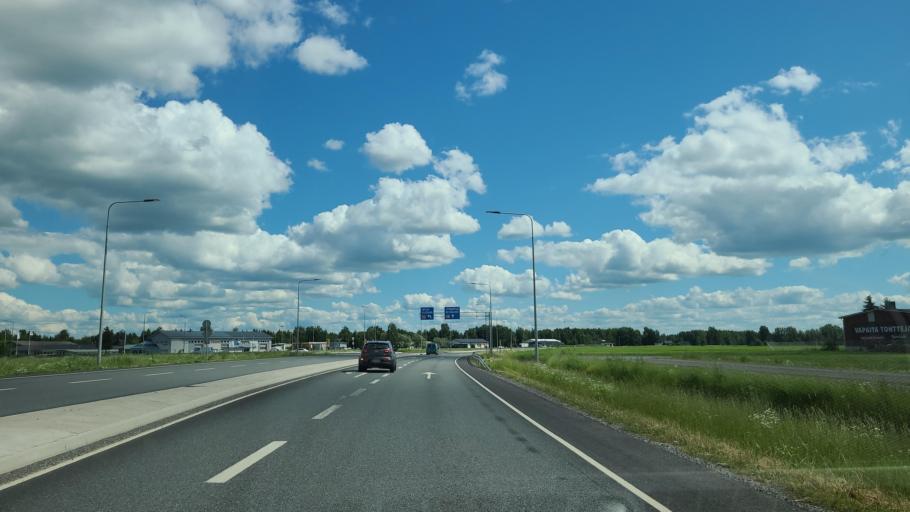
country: FI
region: Southern Ostrobothnia
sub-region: Seinaejoki
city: Ylistaro
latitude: 62.9345
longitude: 22.5020
